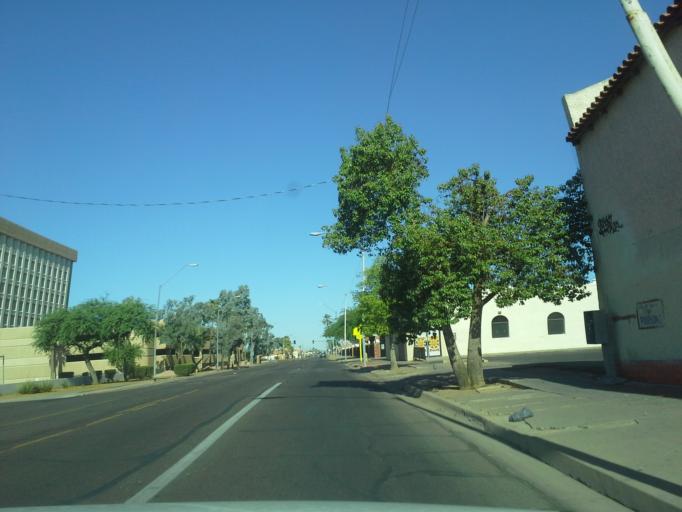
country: US
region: Arizona
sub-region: Maricopa County
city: Phoenix
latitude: 33.4514
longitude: -112.0932
